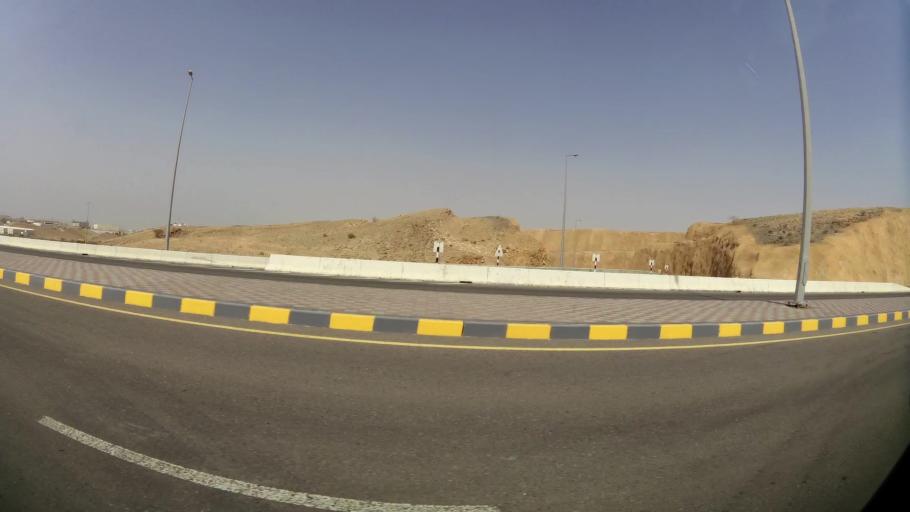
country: OM
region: Muhafazat Masqat
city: Bawshar
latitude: 23.5599
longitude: 58.3387
